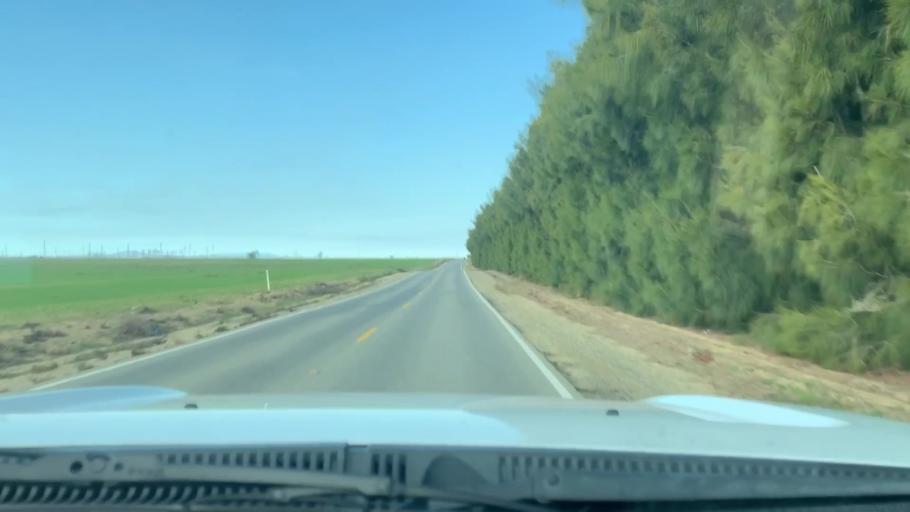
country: US
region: California
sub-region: Kern County
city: Lost Hills
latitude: 35.5100
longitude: -119.7476
